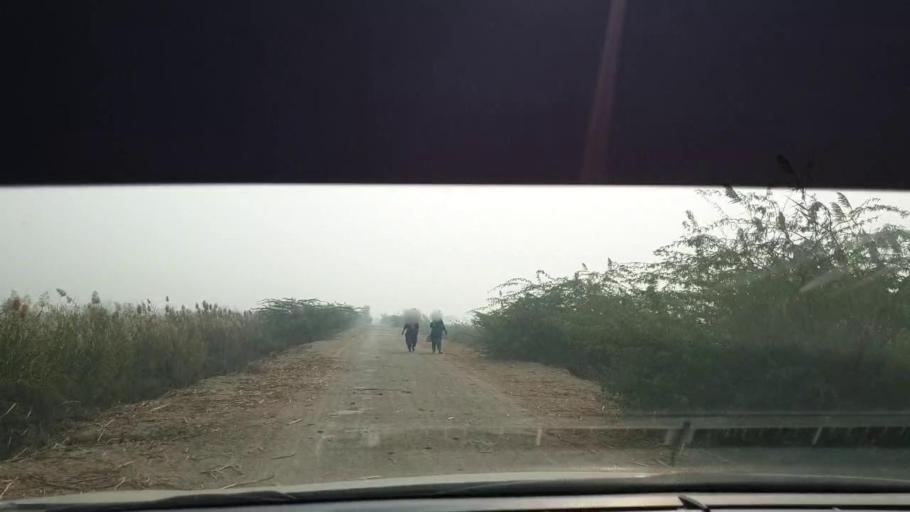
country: PK
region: Sindh
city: Berani
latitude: 25.8388
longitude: 68.8349
